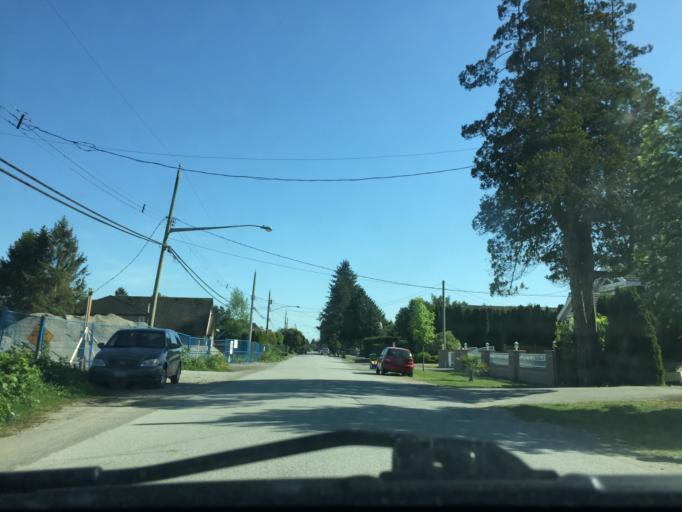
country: CA
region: British Columbia
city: Richmond
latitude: 49.1612
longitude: -123.1171
